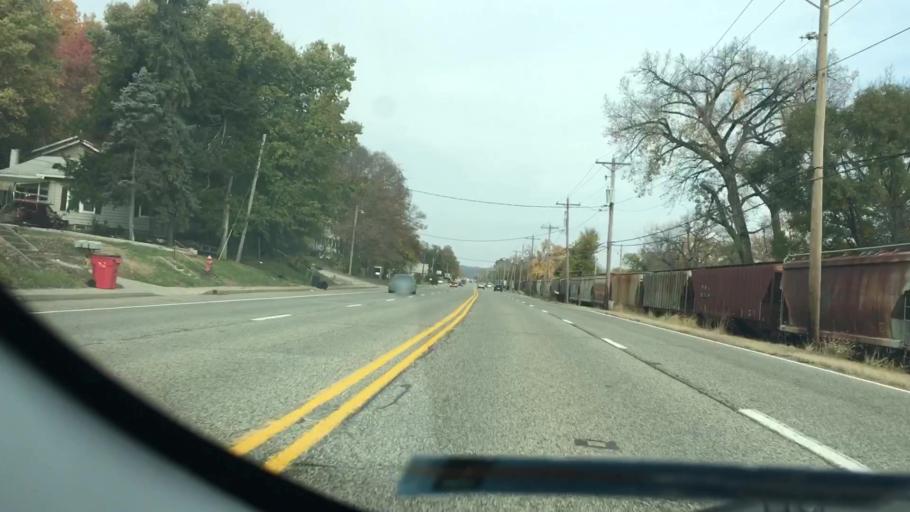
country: US
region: Illinois
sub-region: Peoria County
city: Peoria Heights
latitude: 40.7434
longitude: -89.5552
